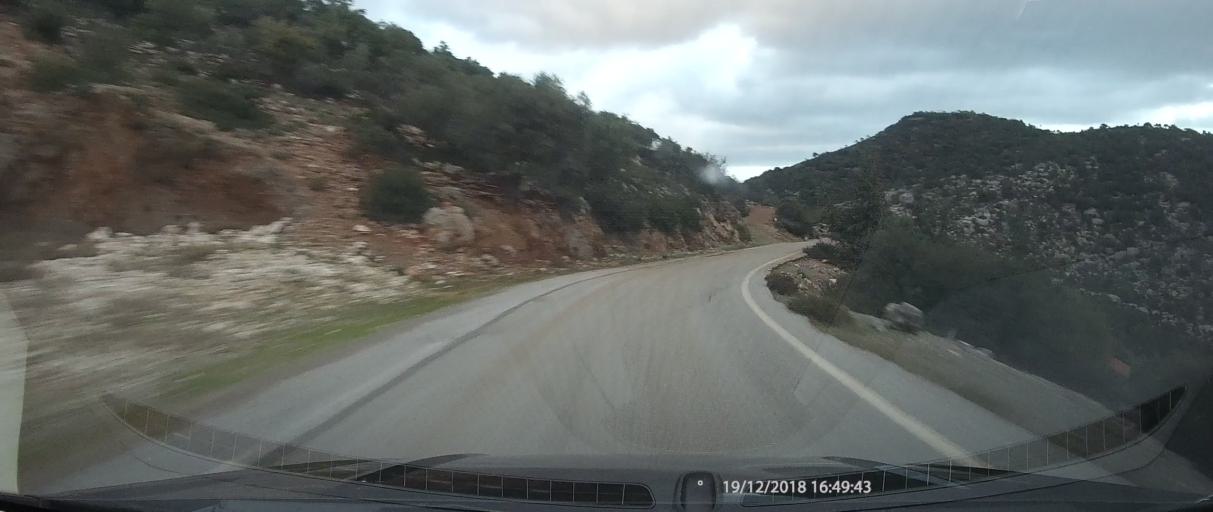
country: GR
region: Peloponnese
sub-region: Nomos Lakonias
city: Sykea
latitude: 36.9486
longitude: 22.9960
